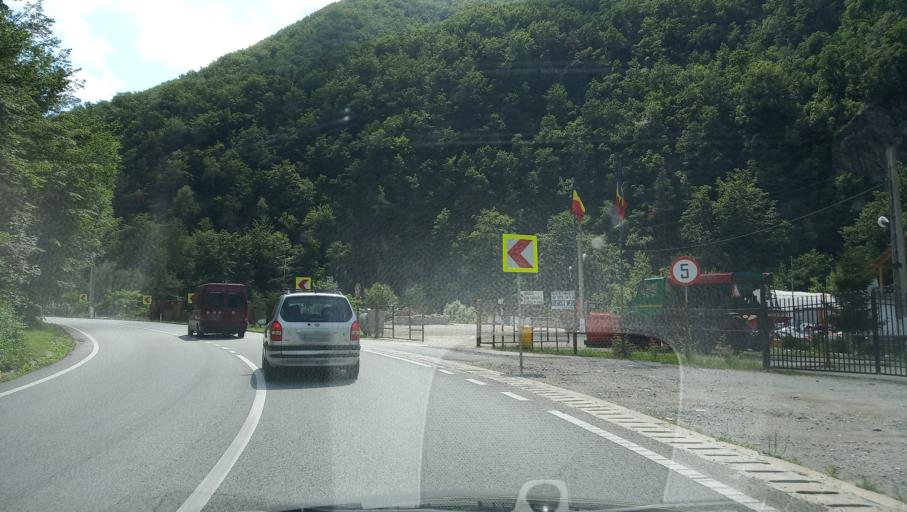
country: RO
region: Gorj
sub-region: Comuna Bumbesti-Jiu
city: Bumbesti-Jiu
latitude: 45.2265
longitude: 23.3831
